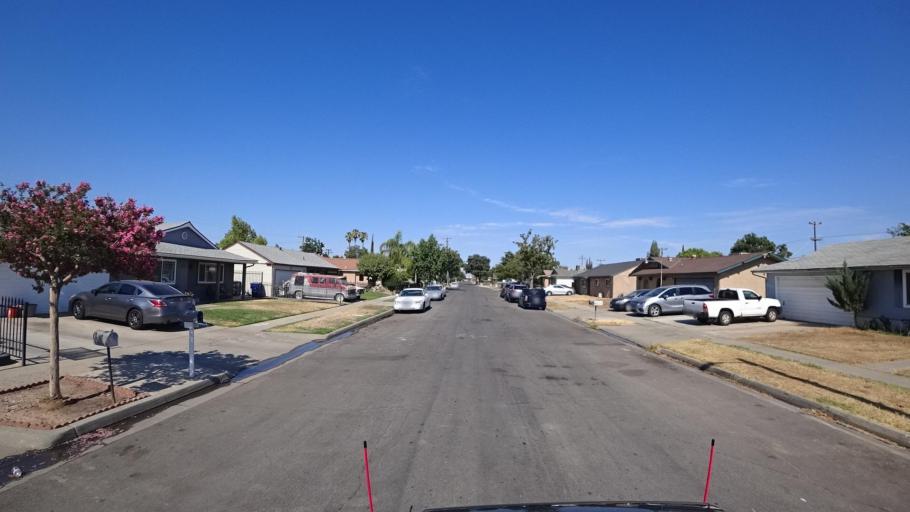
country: US
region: California
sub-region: Fresno County
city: Tarpey Village
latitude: 36.7826
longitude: -119.6846
